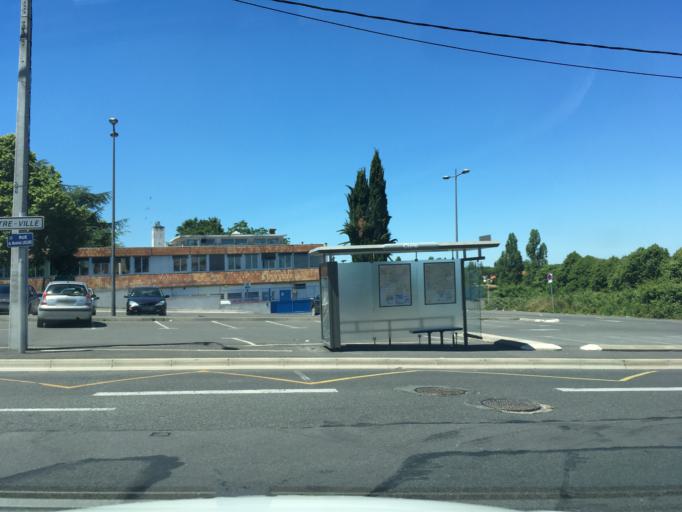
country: FR
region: Poitou-Charentes
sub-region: Departement des Deux-Sevres
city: Niort
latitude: 46.3349
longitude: -0.4533
